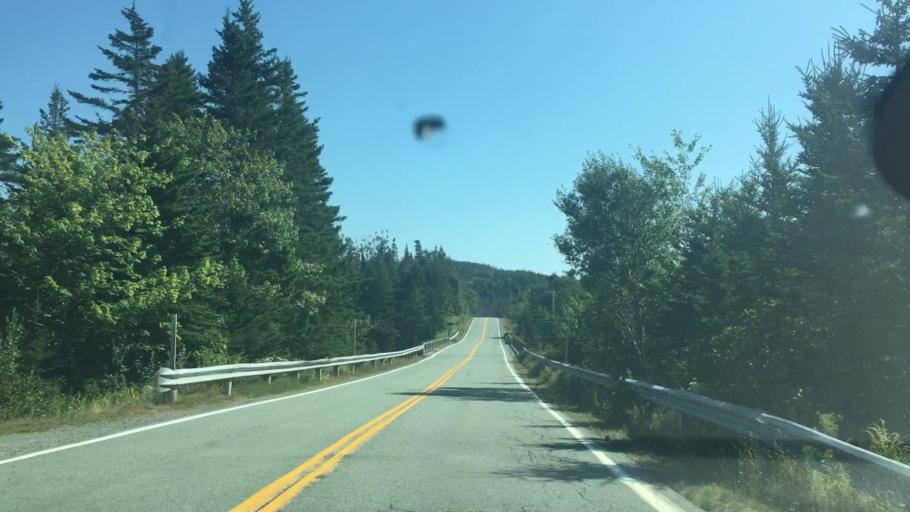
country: CA
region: Nova Scotia
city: Antigonish
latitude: 45.0130
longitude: -62.0982
